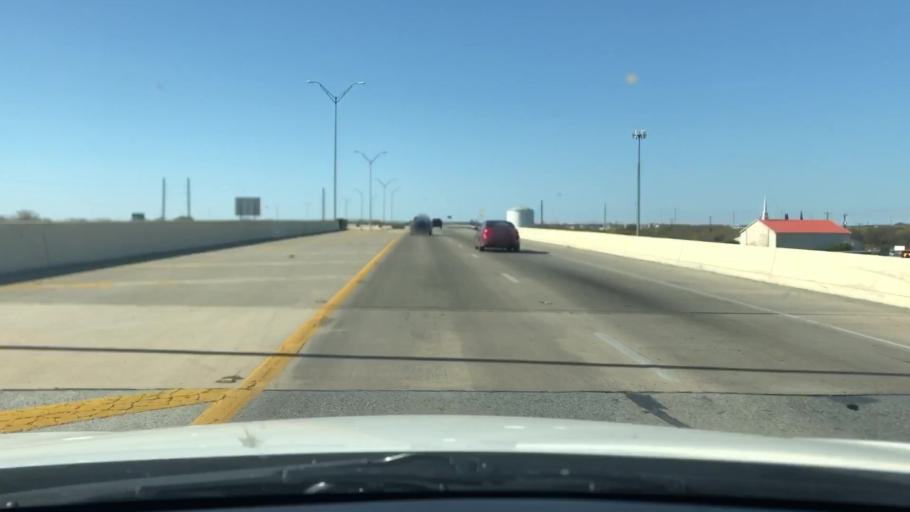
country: US
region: Texas
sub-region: Bexar County
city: Lackland Air Force Base
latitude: 29.4346
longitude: -98.6233
